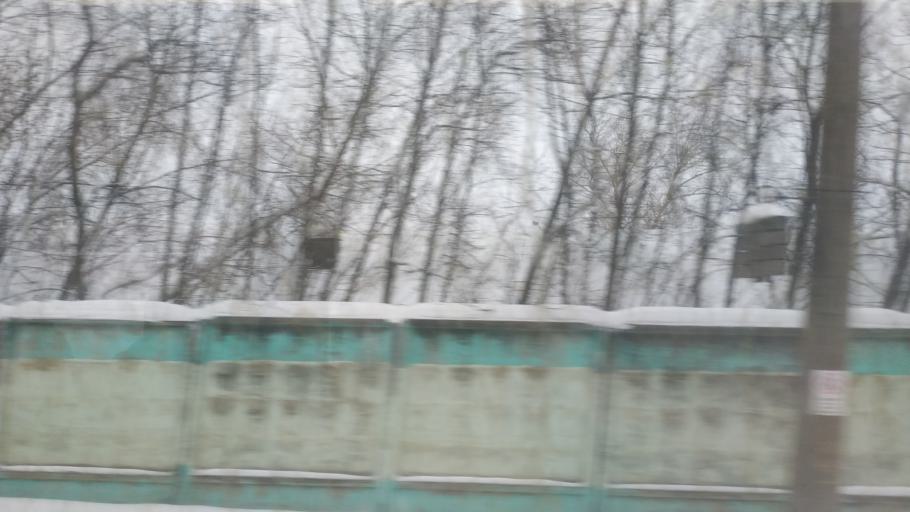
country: RU
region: Moskovskaya
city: Ramenskoye
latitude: 55.5560
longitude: 38.2521
